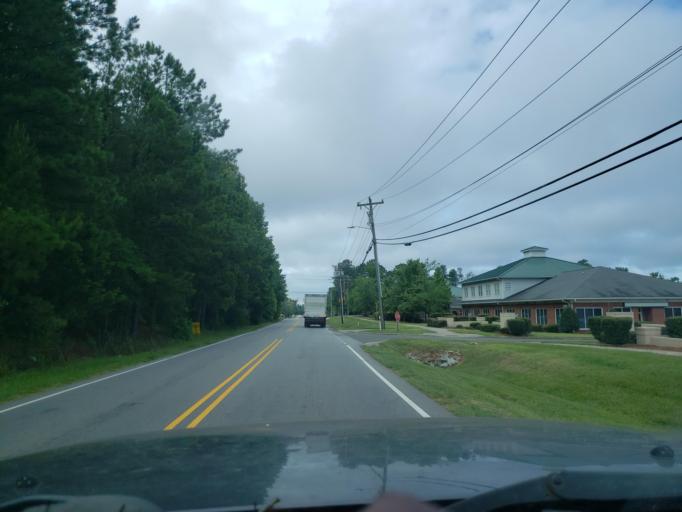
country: US
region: North Carolina
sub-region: Wake County
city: Morrisville
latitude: 35.9279
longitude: -78.8128
